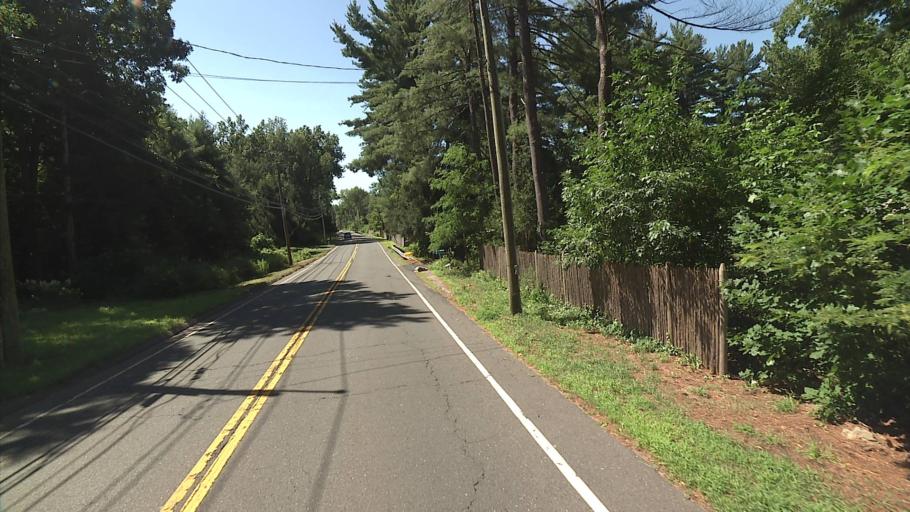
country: US
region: Connecticut
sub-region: Hartford County
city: Farmington
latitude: 41.7451
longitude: -72.8200
